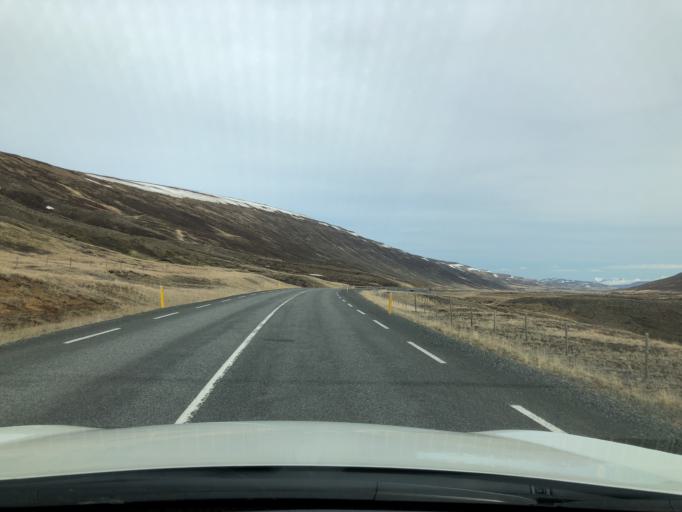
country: IS
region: East
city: Egilsstadir
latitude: 65.3283
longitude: -15.0817
